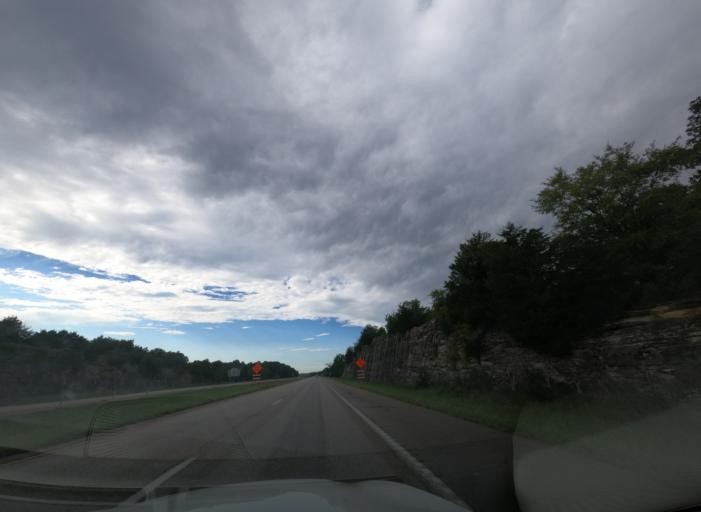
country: US
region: Missouri
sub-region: Sainte Genevieve County
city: Sainte Genevieve
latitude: 37.9825
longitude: -90.1962
